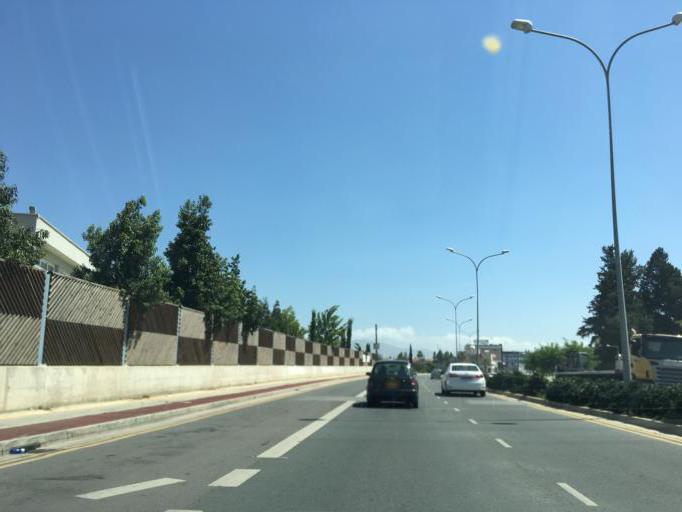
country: CY
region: Lefkosia
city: Nicosia
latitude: 35.1533
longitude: 33.3292
